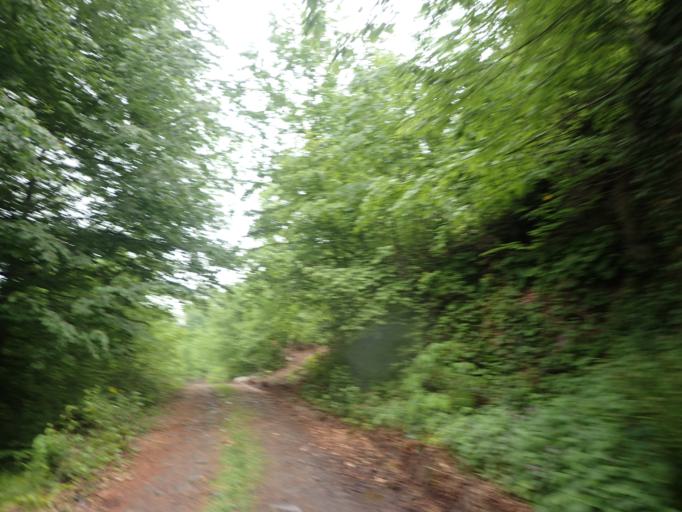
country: TR
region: Ordu
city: Akkus
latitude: 40.8731
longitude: 37.0881
